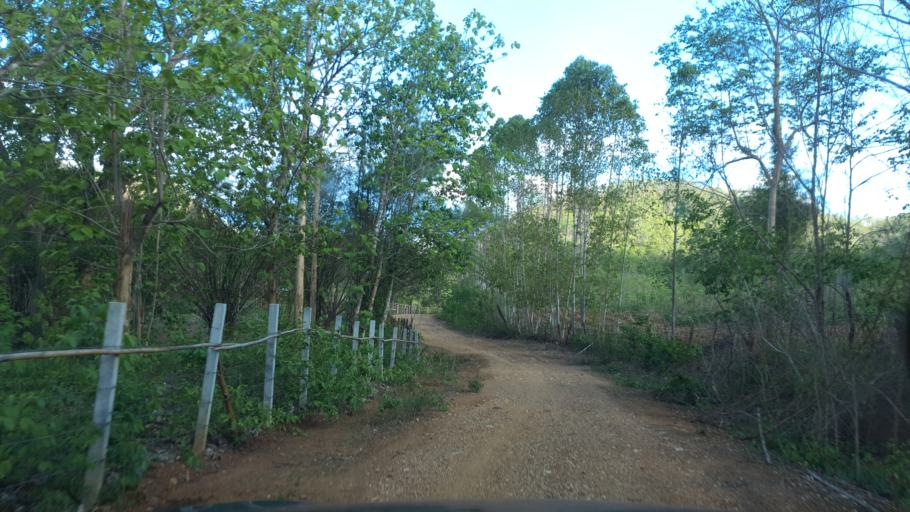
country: TH
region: Lampang
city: Sop Prap
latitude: 17.8496
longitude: 99.2847
